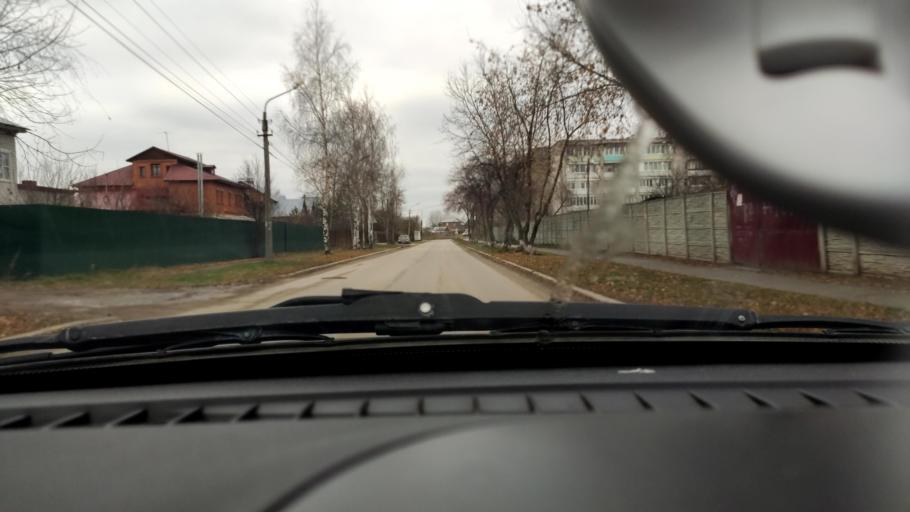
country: RU
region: Perm
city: Kondratovo
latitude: 57.9742
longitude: 56.1062
